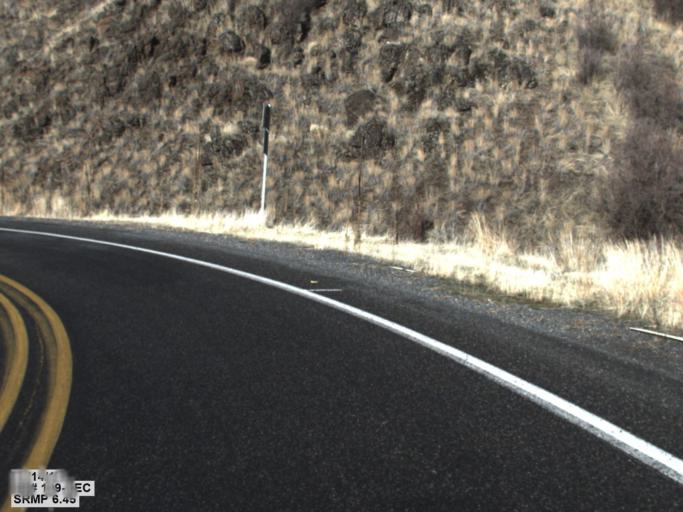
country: US
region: Washington
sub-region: Asotin County
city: Asotin
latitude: 46.0505
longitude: -117.2354
